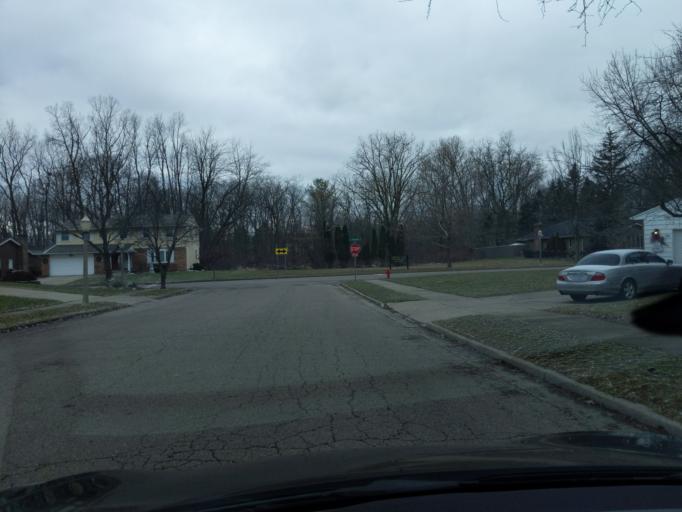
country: US
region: Michigan
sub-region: Ingham County
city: East Lansing
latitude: 42.7522
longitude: -84.5105
